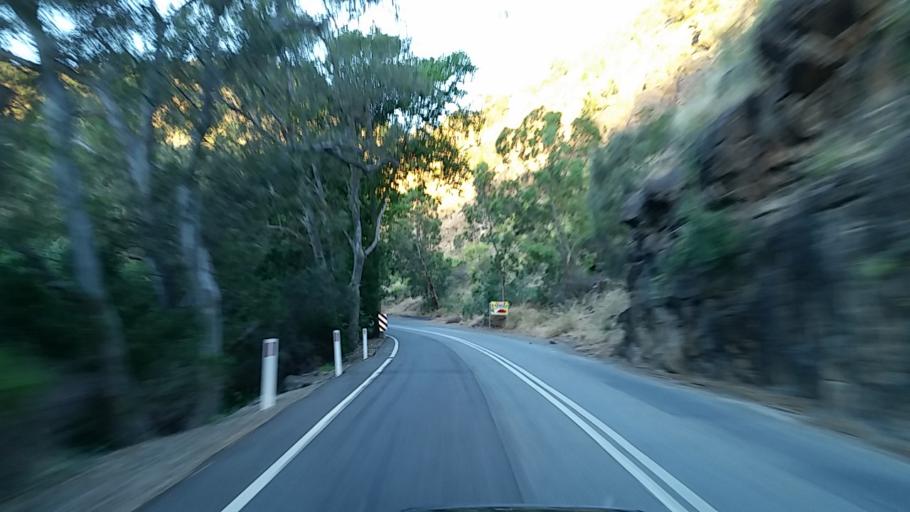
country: AU
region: South Australia
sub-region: Campbelltown
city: Athelstone
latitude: -34.8594
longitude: 138.7293
